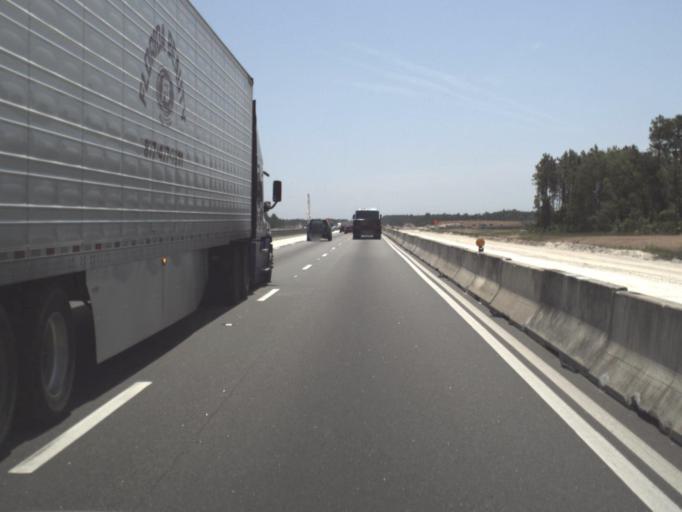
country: US
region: Florida
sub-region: Saint Johns County
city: Fruit Cove
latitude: 30.1212
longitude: -81.5209
